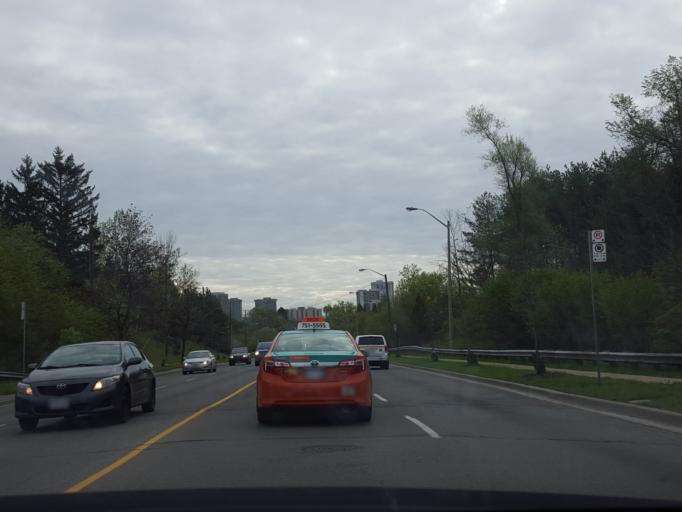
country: CA
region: Ontario
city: Willowdale
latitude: 43.7878
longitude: -79.3793
